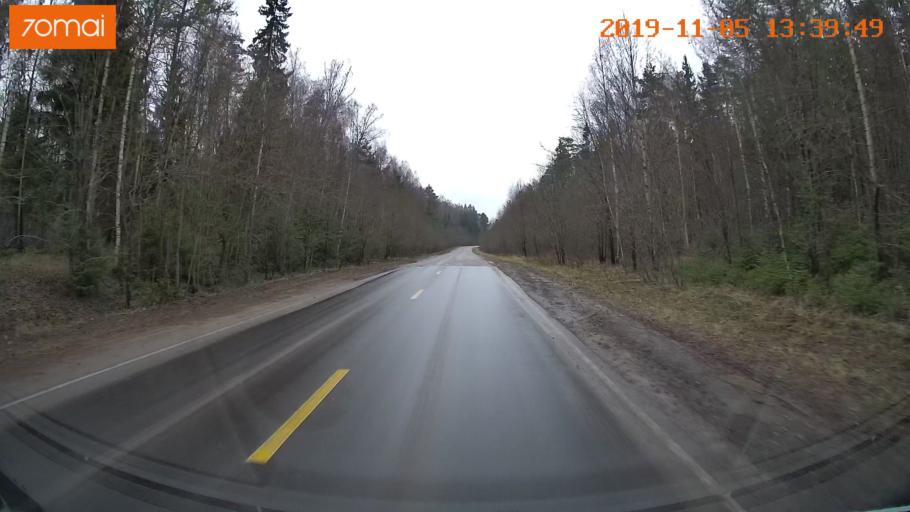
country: RU
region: Ivanovo
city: Shuya
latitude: 56.9433
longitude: 41.3843
